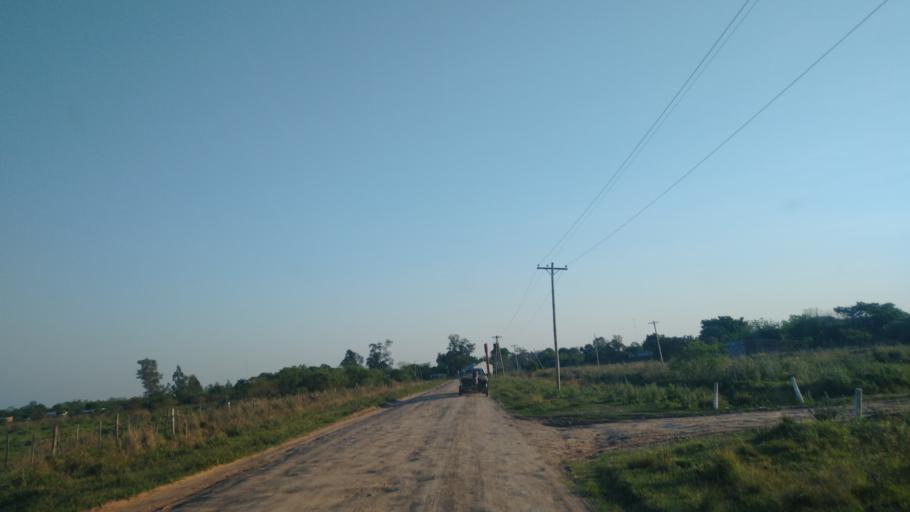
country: PY
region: Neembucu
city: Cerrito
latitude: -27.3771
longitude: -57.6553
